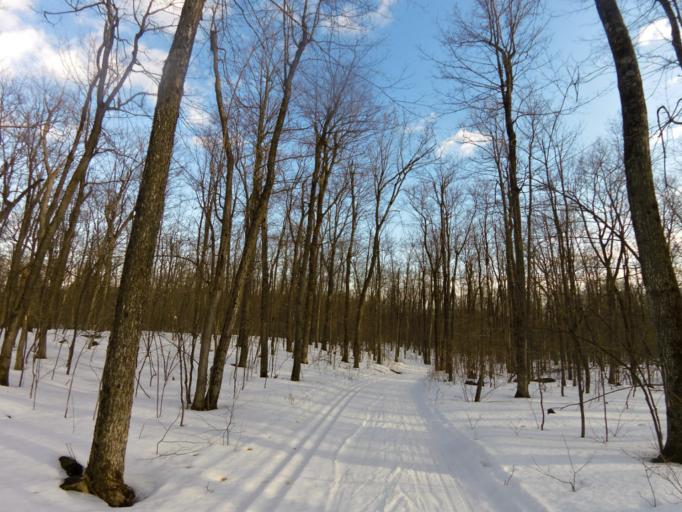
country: CA
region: Quebec
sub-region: Outaouais
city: Gatineau
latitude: 45.4752
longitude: -75.8401
